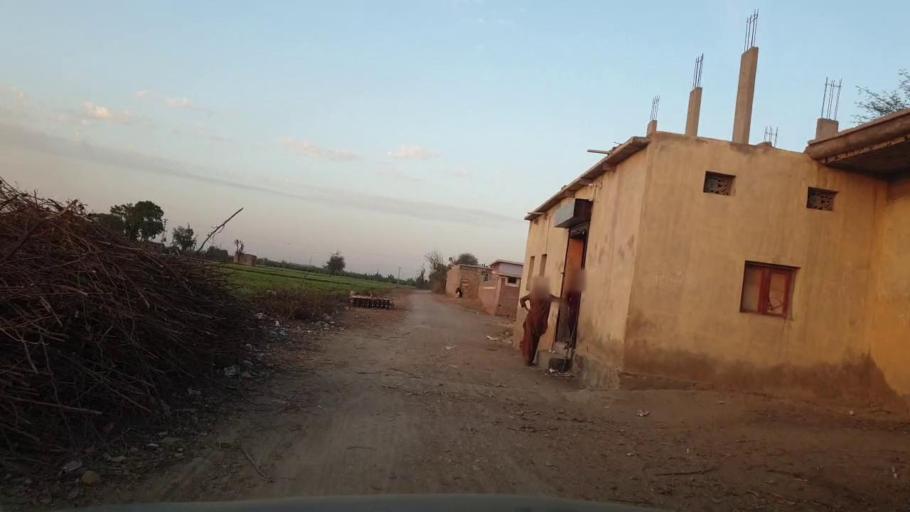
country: PK
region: Sindh
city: Matiari
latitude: 25.6020
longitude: 68.4801
